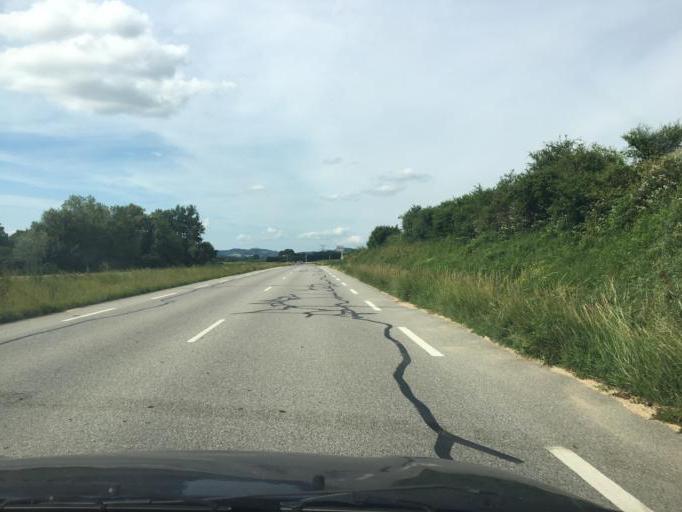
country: FR
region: Rhone-Alpes
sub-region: Departement de la Drome
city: Chanos-Curson
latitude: 45.0756
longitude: 4.9360
